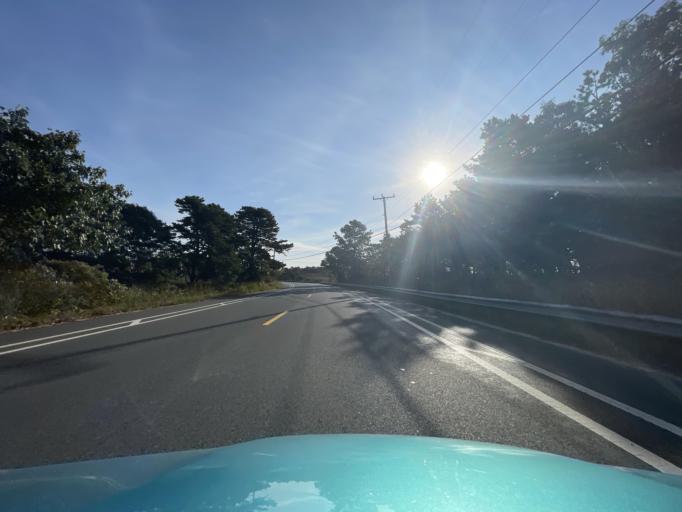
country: US
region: Massachusetts
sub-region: Bristol County
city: Head of Westport
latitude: 41.5076
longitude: -71.0521
